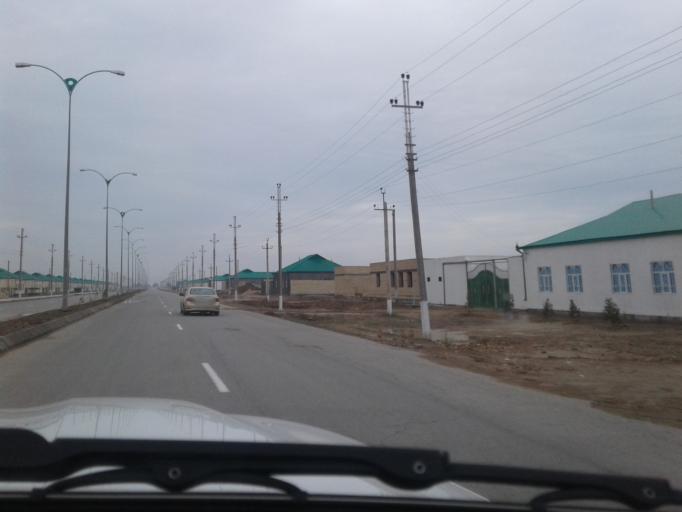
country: TM
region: Mary
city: Bayramaly
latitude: 37.6345
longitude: 62.1463
